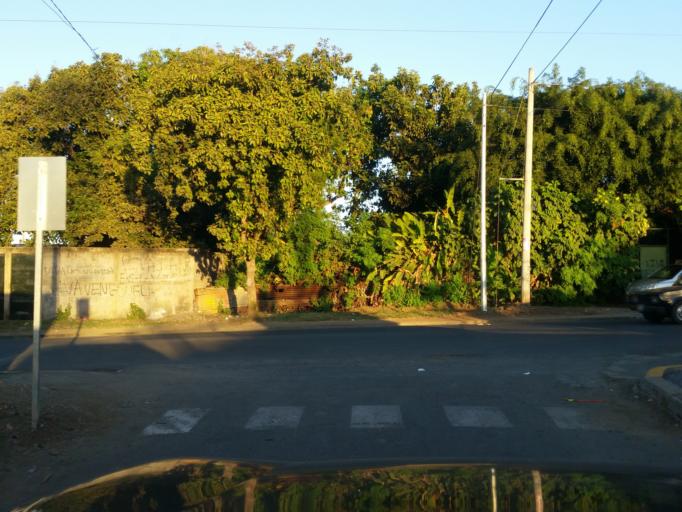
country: NI
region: Managua
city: Managua
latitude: 12.1043
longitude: -86.2334
